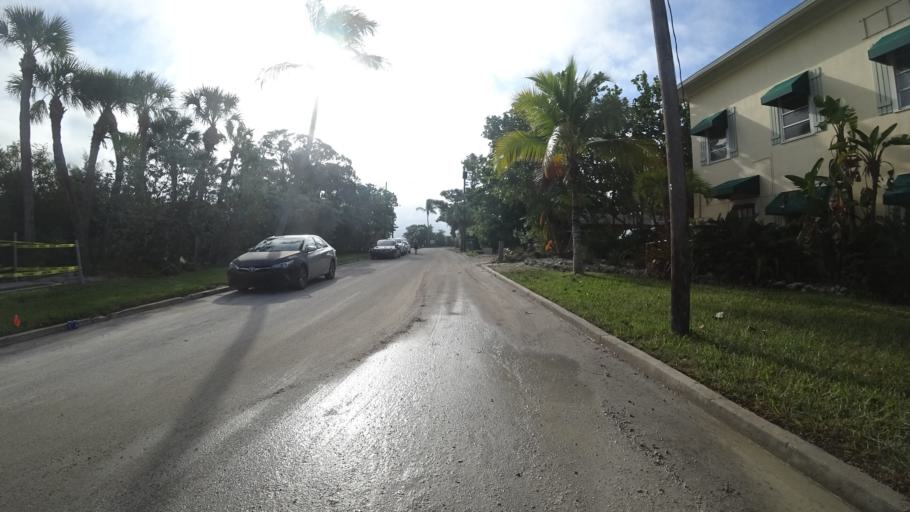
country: US
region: Florida
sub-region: Manatee County
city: Cortez
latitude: 27.4380
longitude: -82.6819
